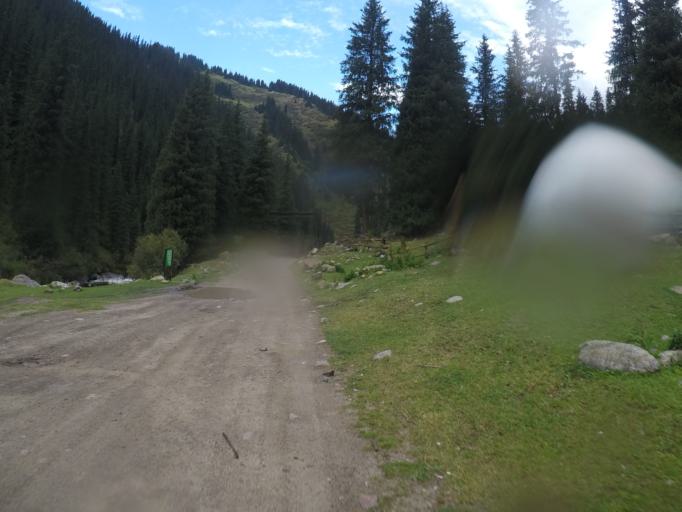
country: KG
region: Ysyk-Koel
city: Teploklyuchenka
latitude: 42.4130
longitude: 78.5741
